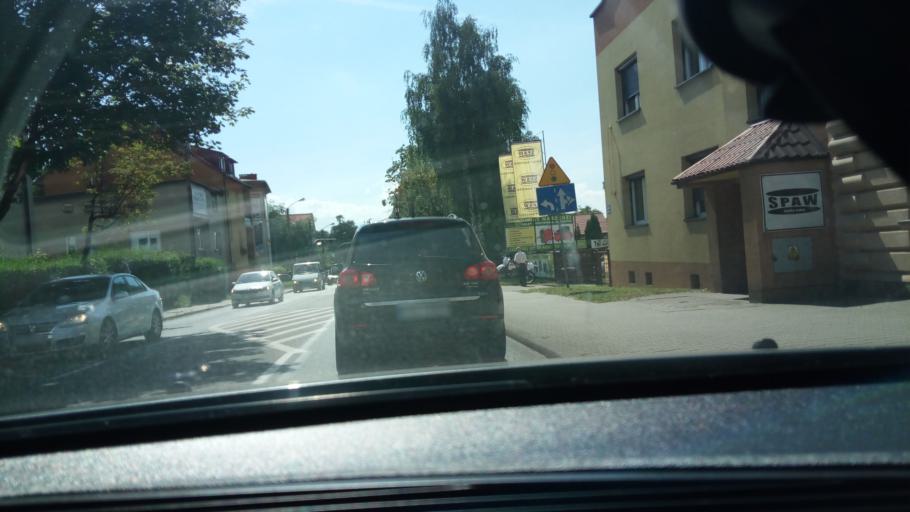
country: PL
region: Lesser Poland Voivodeship
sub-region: Powiat chrzanowski
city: Chrzanow
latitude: 50.1421
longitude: 19.3977
